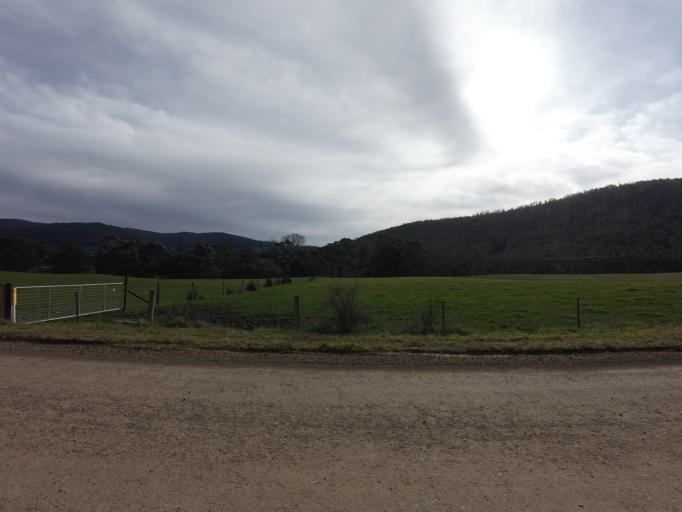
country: AU
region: Tasmania
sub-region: Huon Valley
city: Huonville
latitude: -43.0724
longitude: 147.0474
